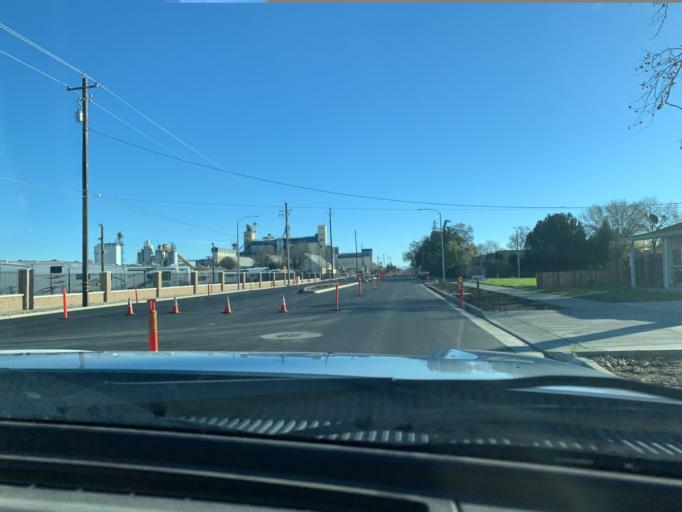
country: US
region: California
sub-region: Yolo County
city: Woodland
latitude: 38.6919
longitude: -121.7716
